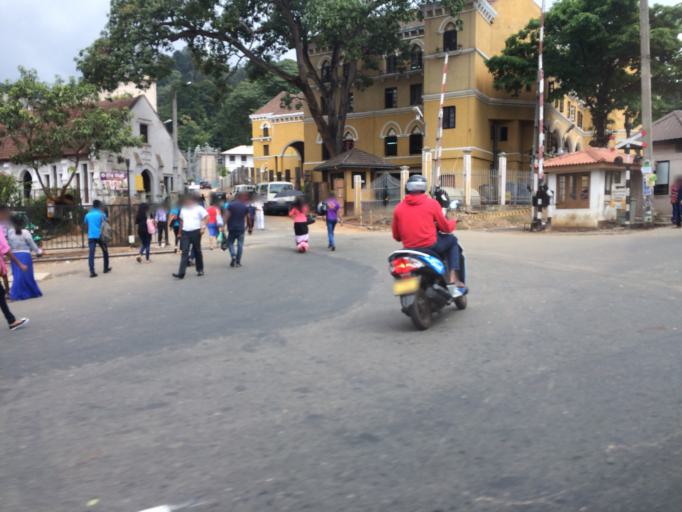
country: LK
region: Central
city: Kandy
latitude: 7.2922
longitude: 80.6338
